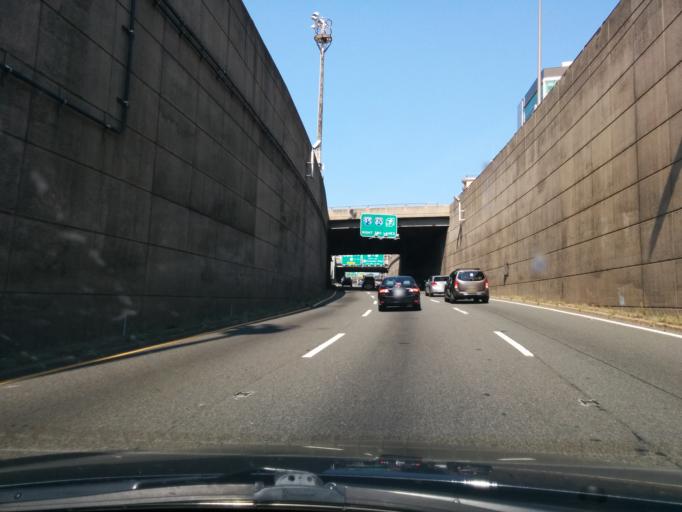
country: US
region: New Jersey
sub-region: Bergen County
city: Fort Lee
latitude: 40.8547
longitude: -73.9655
